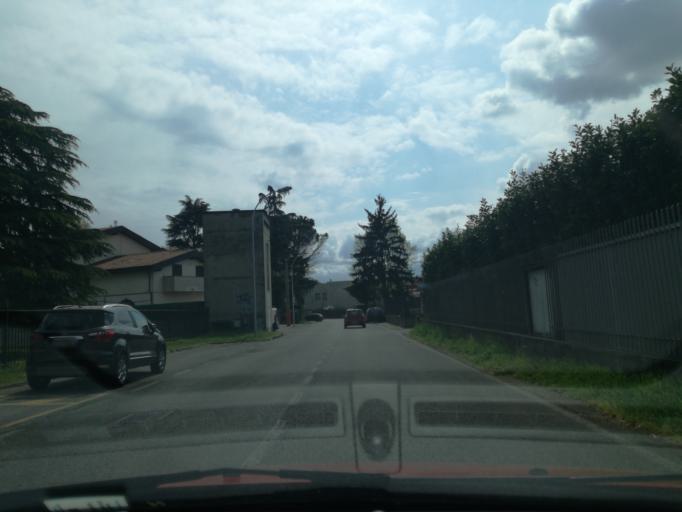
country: IT
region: Lombardy
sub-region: Provincia di Monza e Brianza
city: Carate Brianza
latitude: 45.6675
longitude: 9.2293
